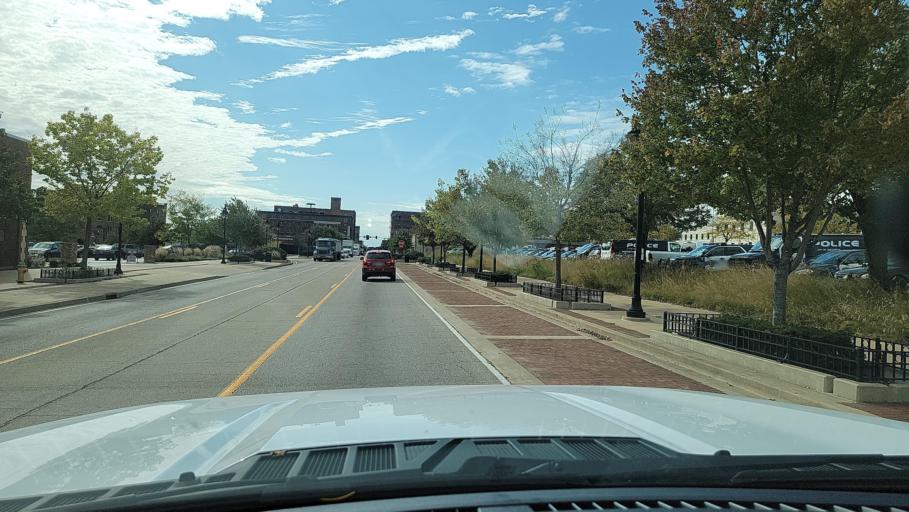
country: US
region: Illinois
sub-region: Peoria County
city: Peoria
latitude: 40.6871
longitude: -89.5941
